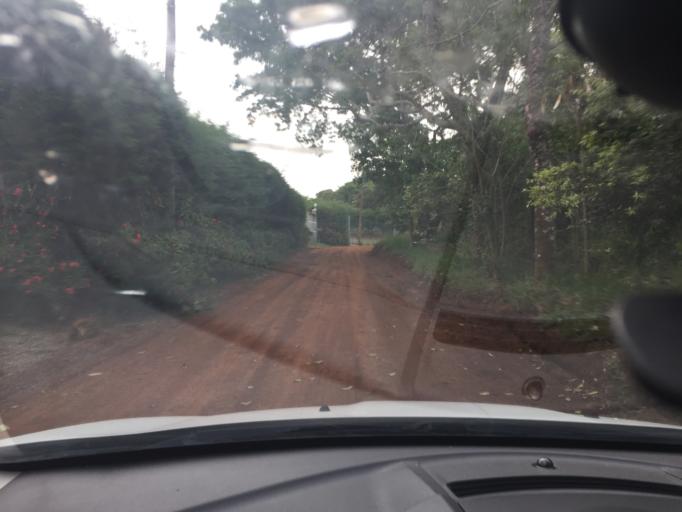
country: BR
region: Sao Paulo
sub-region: Campo Limpo Paulista
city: Campo Limpo Paulista
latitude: -23.1593
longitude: -46.7914
